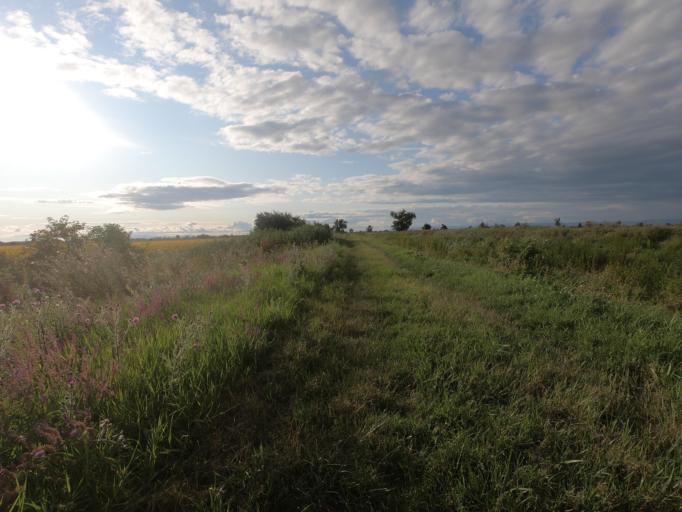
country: HU
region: Heves
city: Poroszlo
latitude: 47.7075
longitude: 20.5806
